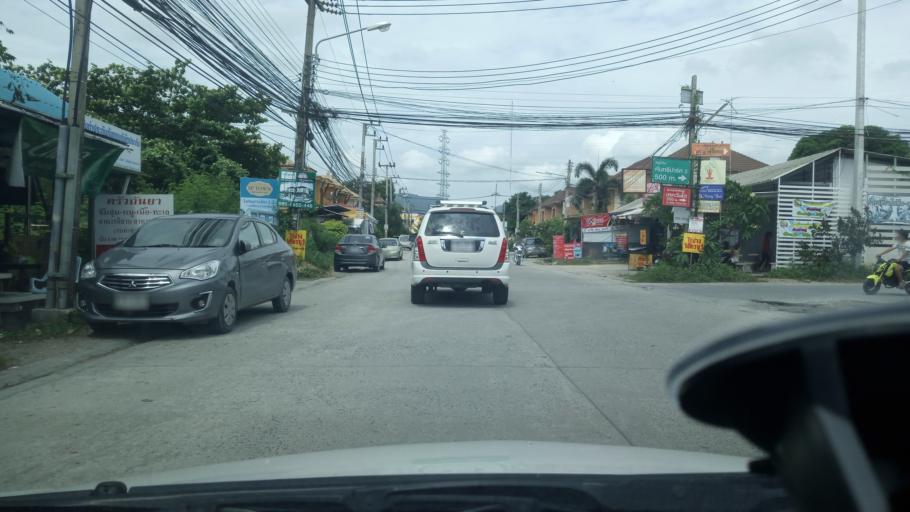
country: TH
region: Chon Buri
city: Chon Buri
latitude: 13.2975
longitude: 100.9519
